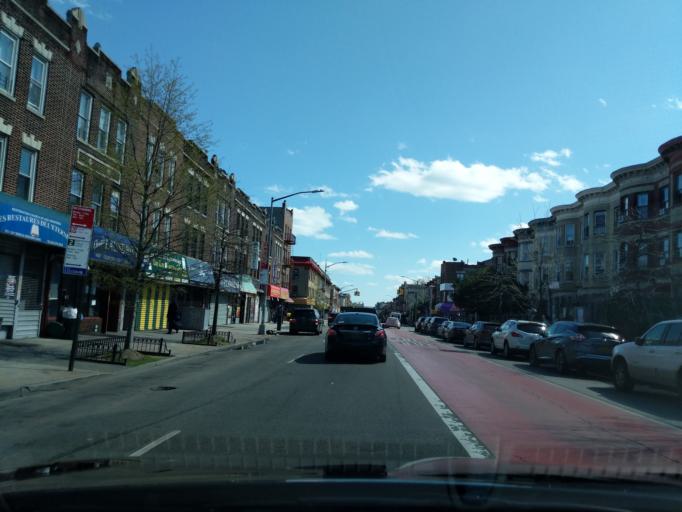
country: US
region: New York
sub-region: Kings County
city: Brooklyn
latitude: 40.6459
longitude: -73.9490
